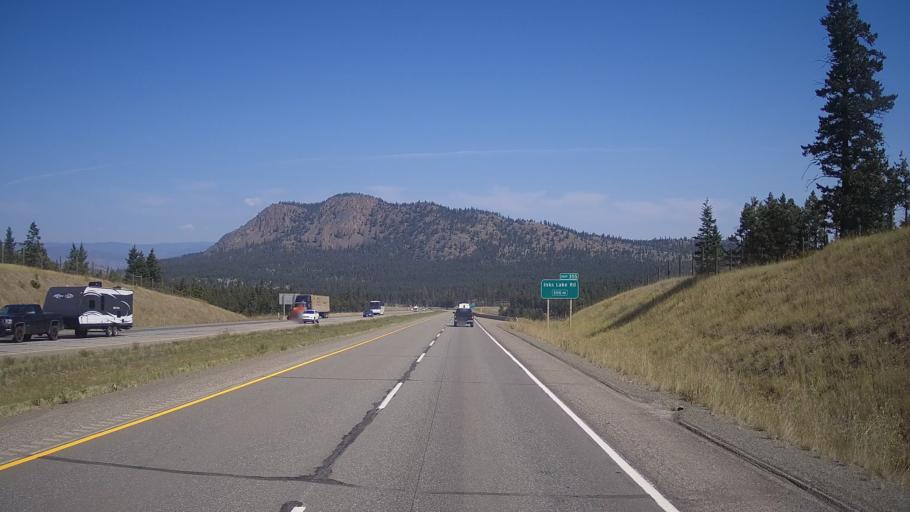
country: CA
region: British Columbia
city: Kamloops
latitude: 50.6133
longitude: -120.4727
